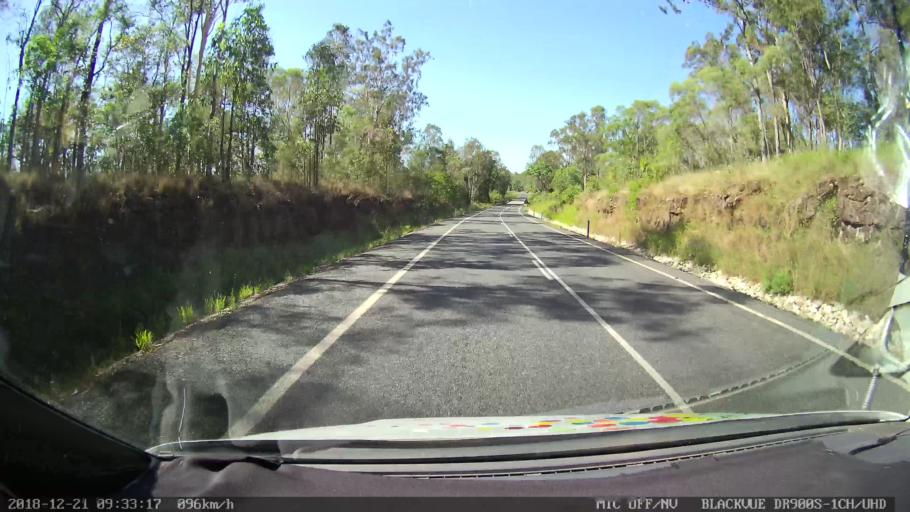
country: AU
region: New South Wales
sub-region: Clarence Valley
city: Grafton
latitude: -29.4823
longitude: 152.9768
